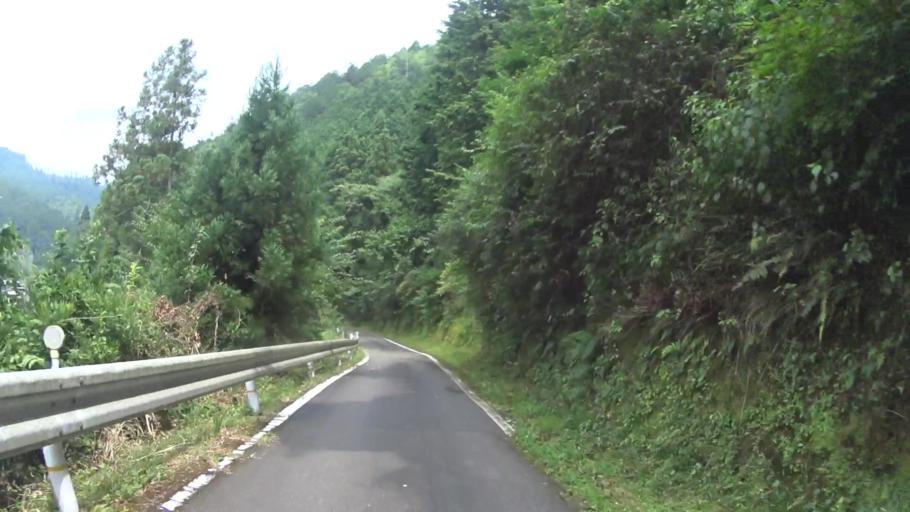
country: JP
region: Kyoto
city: Kameoka
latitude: 35.2047
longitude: 135.5840
